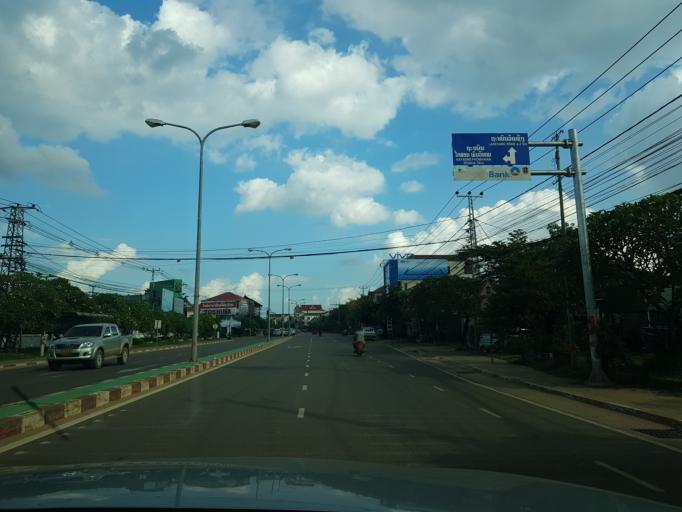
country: TH
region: Nong Khai
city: Si Chiang Mai
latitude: 17.9704
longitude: 102.5710
